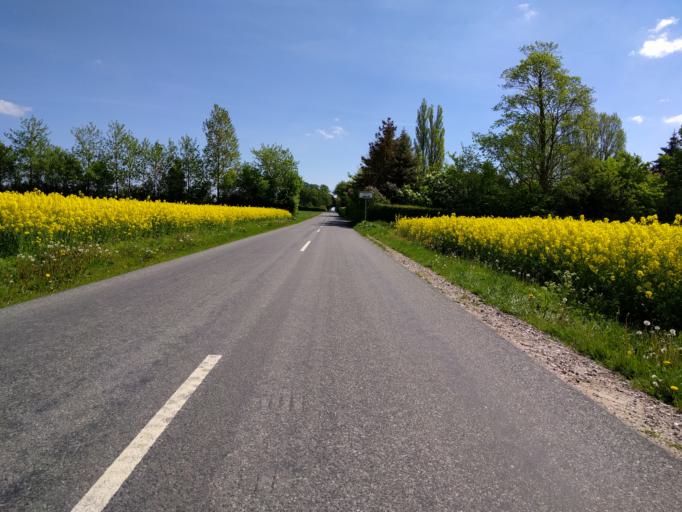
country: DK
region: Zealand
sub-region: Guldborgsund Kommune
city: Nykobing Falster
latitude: 54.7403
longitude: 11.9995
